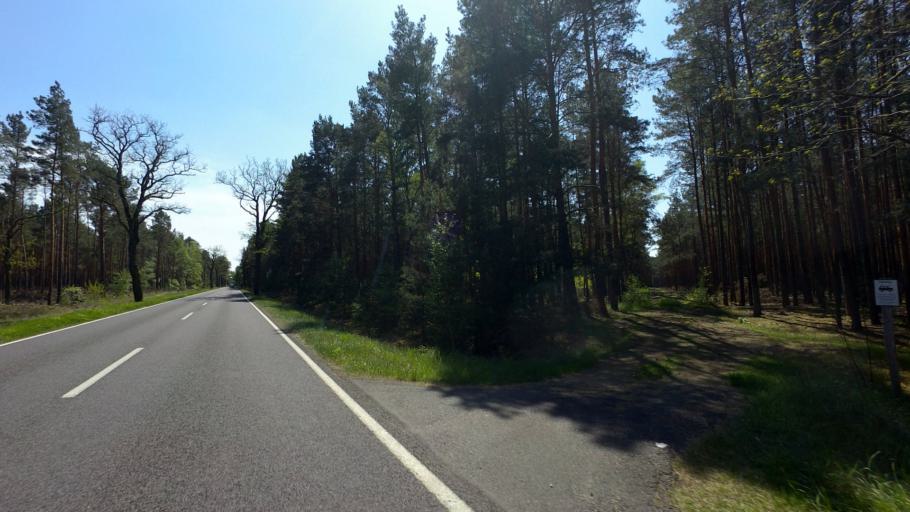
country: DE
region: Brandenburg
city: Halbe
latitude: 52.1671
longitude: 13.7265
